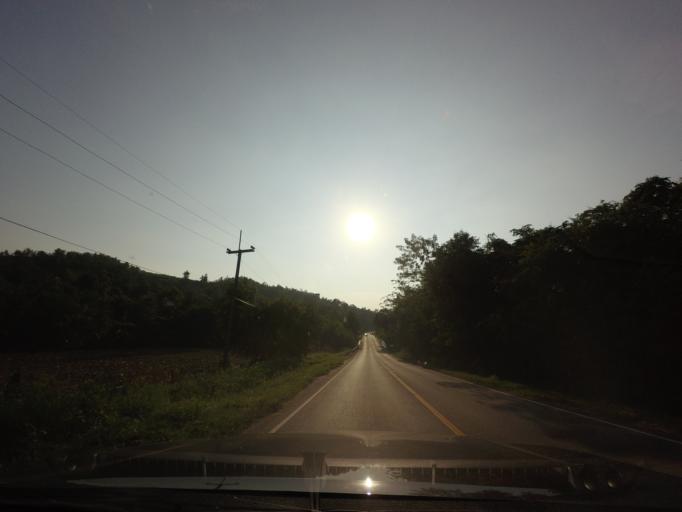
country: TH
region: Nan
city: Na Noi
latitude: 18.3360
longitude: 100.7830
